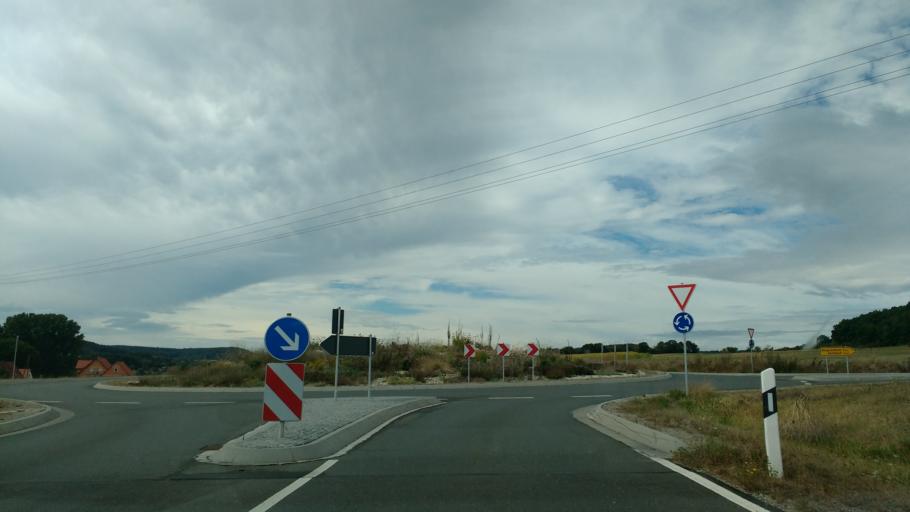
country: DE
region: Bavaria
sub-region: Regierungsbezirk Mittelfranken
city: Burghaslach
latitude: 49.7680
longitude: 10.5508
